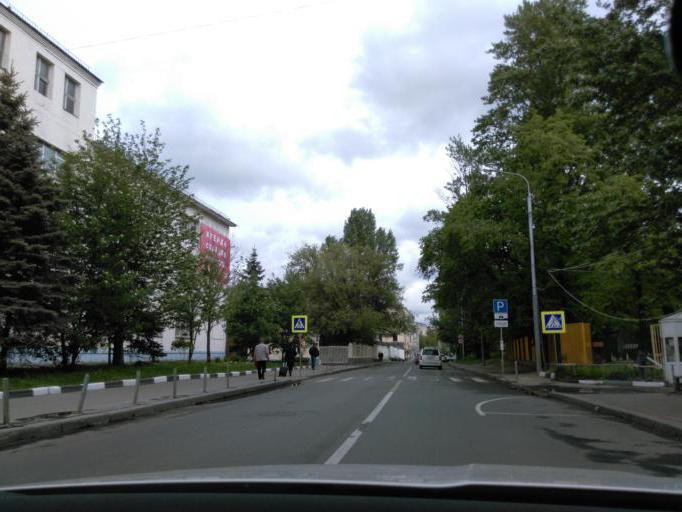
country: RU
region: Moscow
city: Zamoskvorech'ye
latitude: 55.7189
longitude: 37.6475
